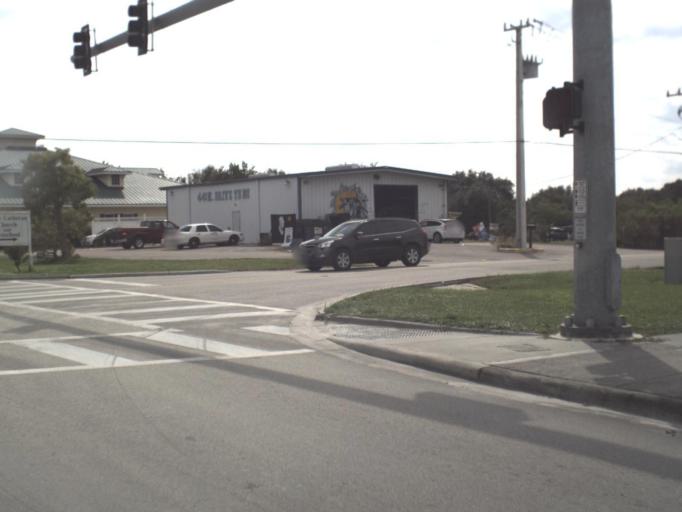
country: US
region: Florida
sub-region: Okeechobee County
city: Cypress Quarters
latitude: 27.2655
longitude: -80.8300
